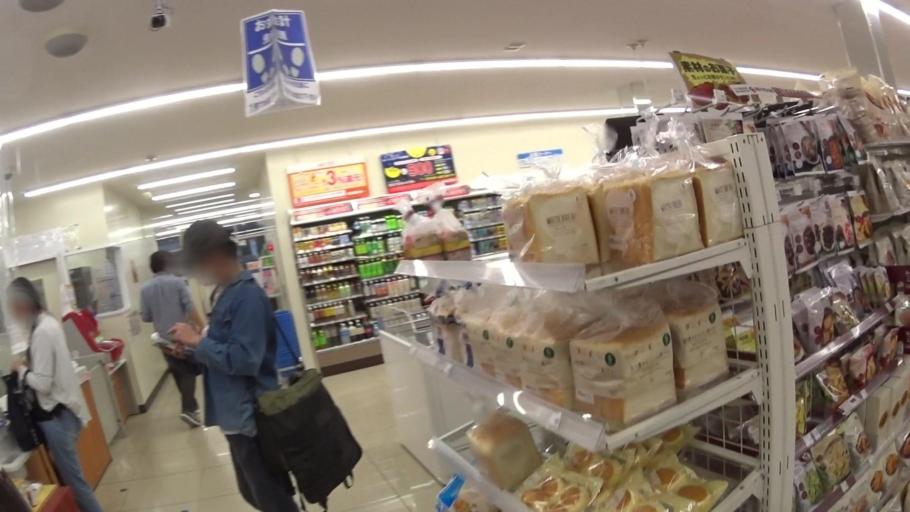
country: JP
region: Osaka
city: Kaizuka
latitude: 34.4555
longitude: 135.2880
